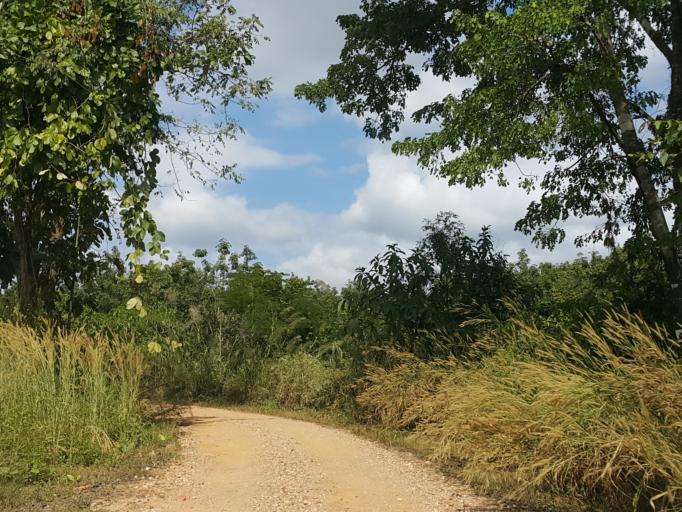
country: TH
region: Lampang
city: Hang Chat
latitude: 18.4825
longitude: 99.4156
